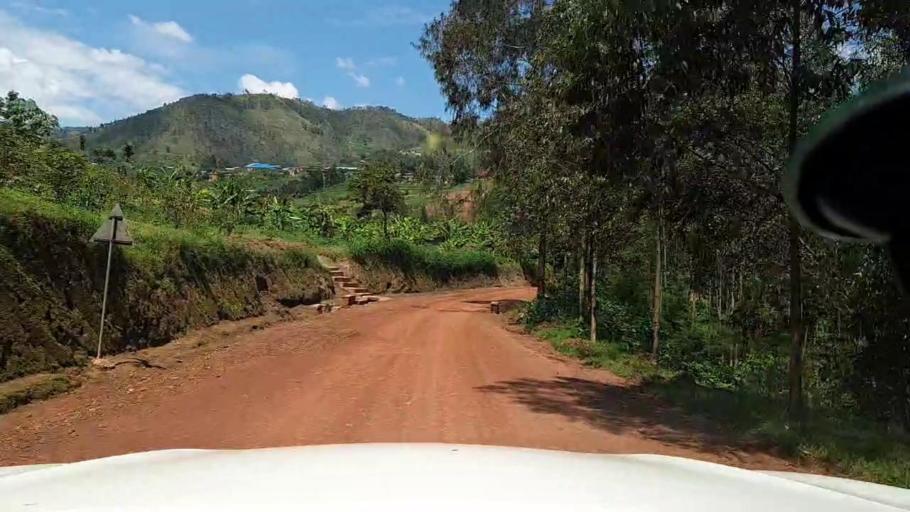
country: RW
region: Kigali
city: Kigali
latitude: -1.7601
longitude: 29.8706
